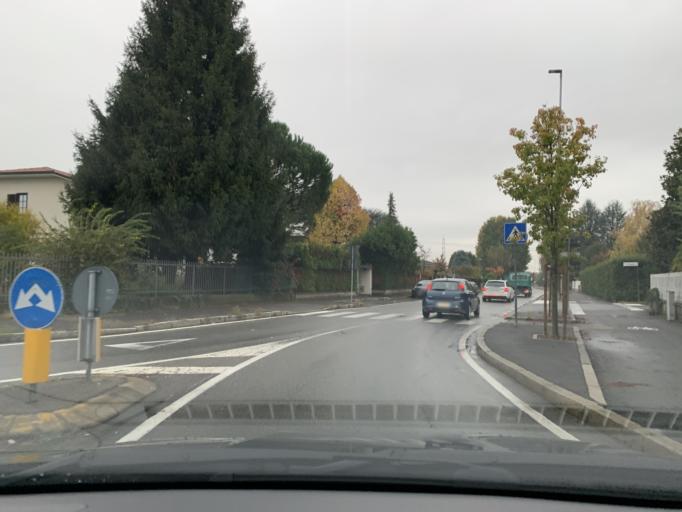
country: IT
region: Lombardy
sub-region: Provincia di Como
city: Rovellasca
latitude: 45.6606
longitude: 9.0533
